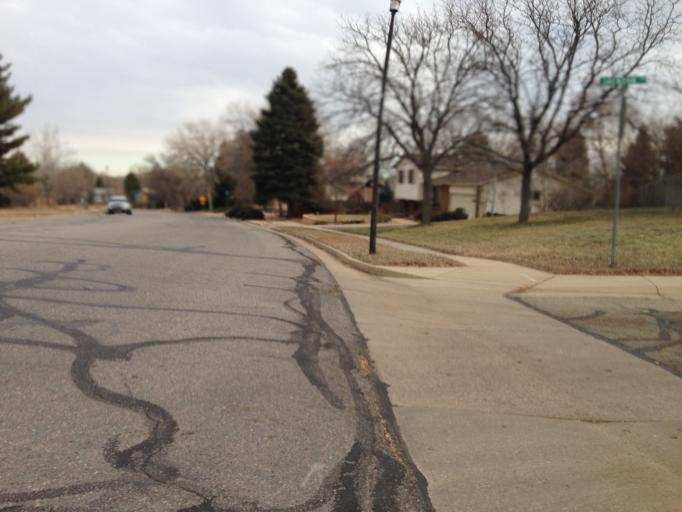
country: US
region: Colorado
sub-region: Boulder County
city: Louisville
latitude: 39.9811
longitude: -105.1443
